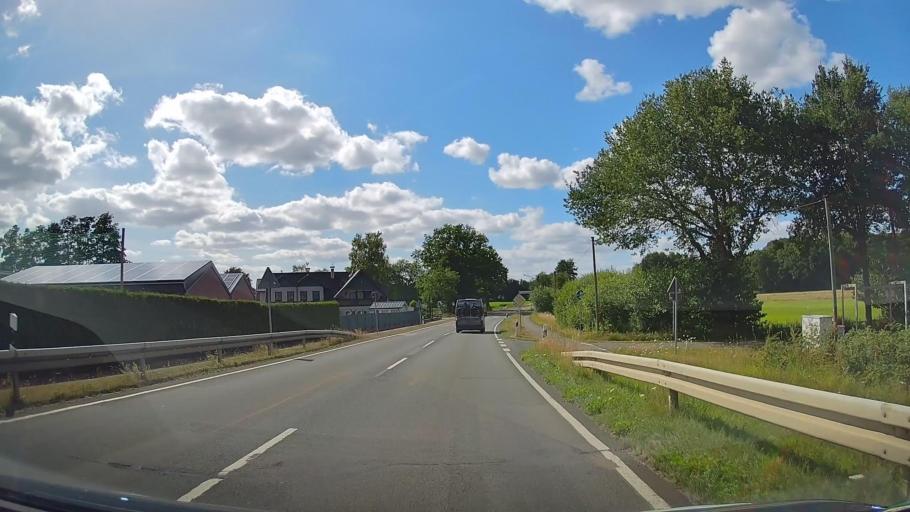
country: DE
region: Lower Saxony
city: Alfhausen
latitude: 52.4996
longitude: 7.9744
